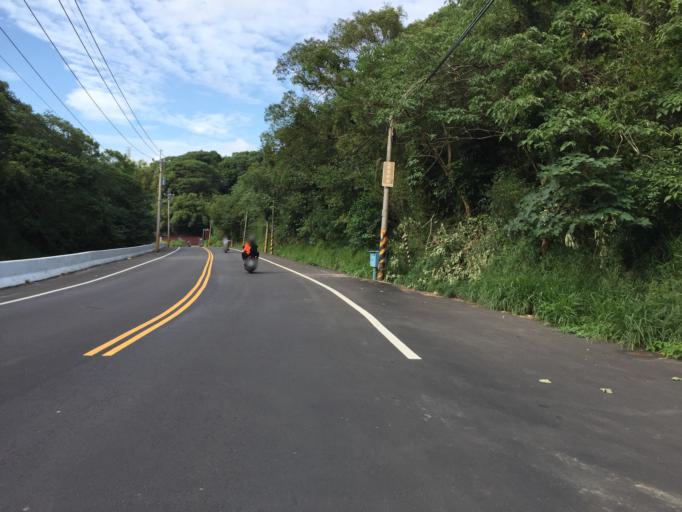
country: TW
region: Taiwan
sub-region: Hsinchu
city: Hsinchu
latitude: 24.7627
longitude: 120.9431
